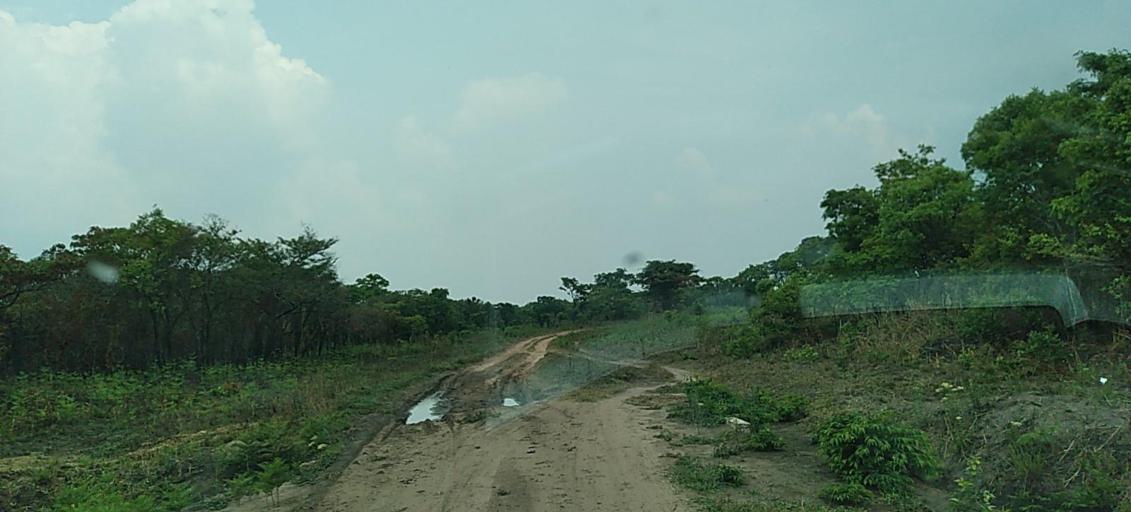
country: ZM
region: North-Western
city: Mwinilunga
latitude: -11.4301
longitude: 24.5920
